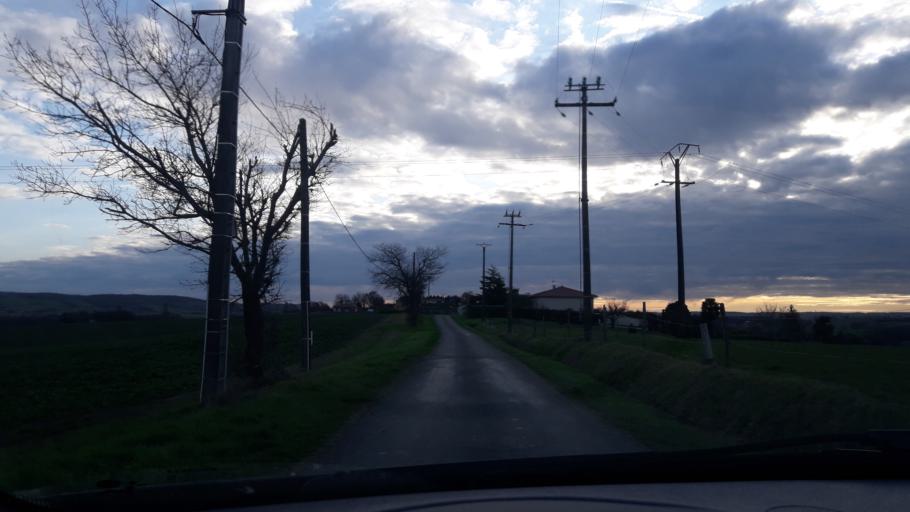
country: FR
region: Midi-Pyrenees
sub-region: Departement du Gers
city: Pujaudran
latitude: 43.6666
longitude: 1.0537
